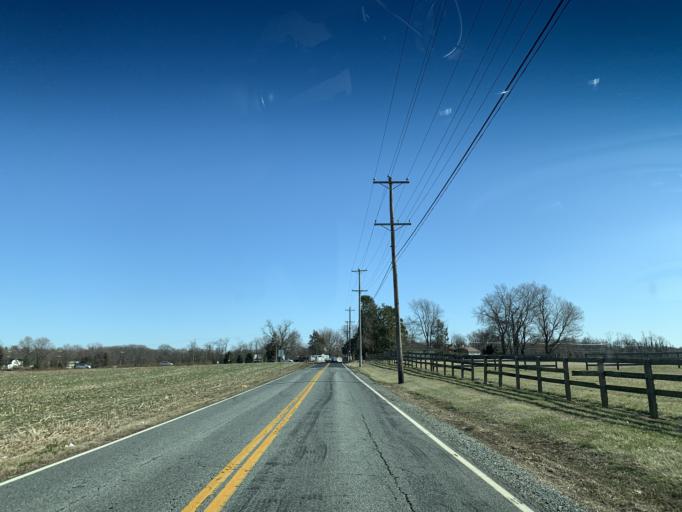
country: US
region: Maryland
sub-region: Cecil County
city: Elkton
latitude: 39.4875
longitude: -75.8504
